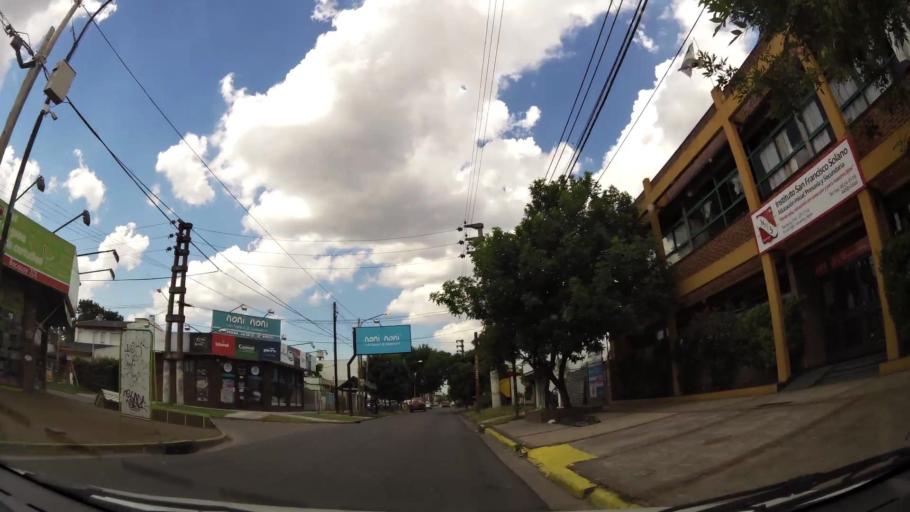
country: AR
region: Buenos Aires
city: Ituzaingo
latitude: -34.6498
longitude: -58.6693
